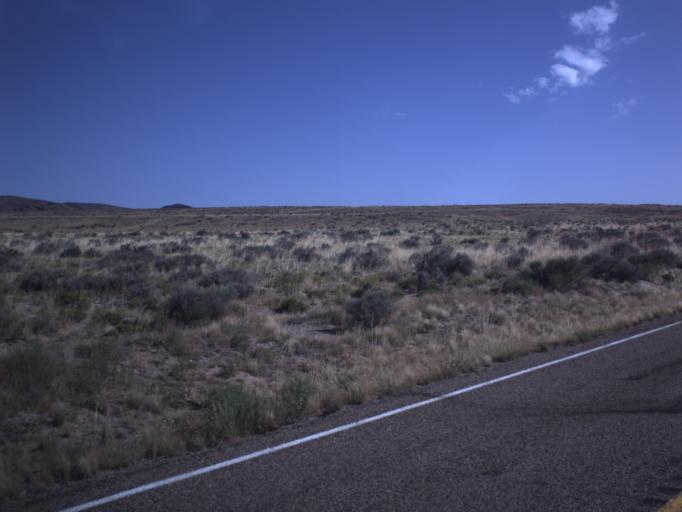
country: US
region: Utah
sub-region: Beaver County
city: Milford
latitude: 38.7595
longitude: -112.9426
